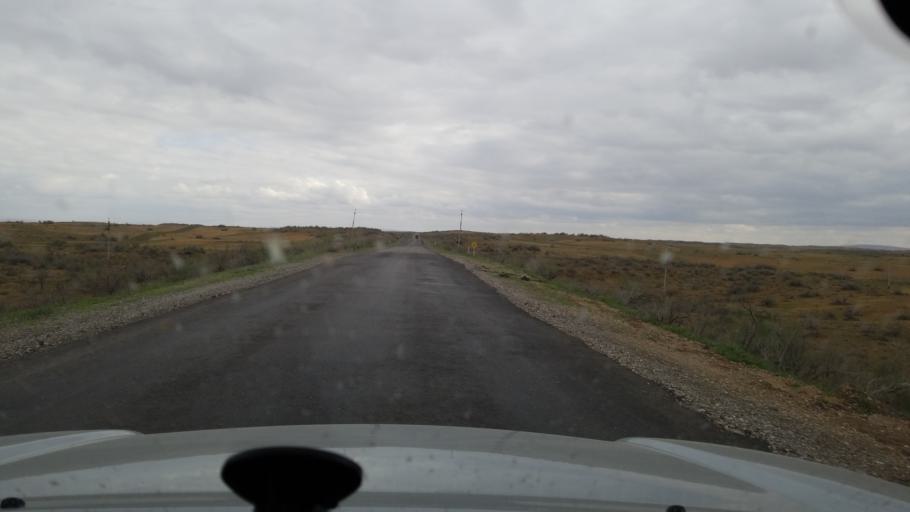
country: TM
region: Mary
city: Serhetabat
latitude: 36.0918
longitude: 62.6120
